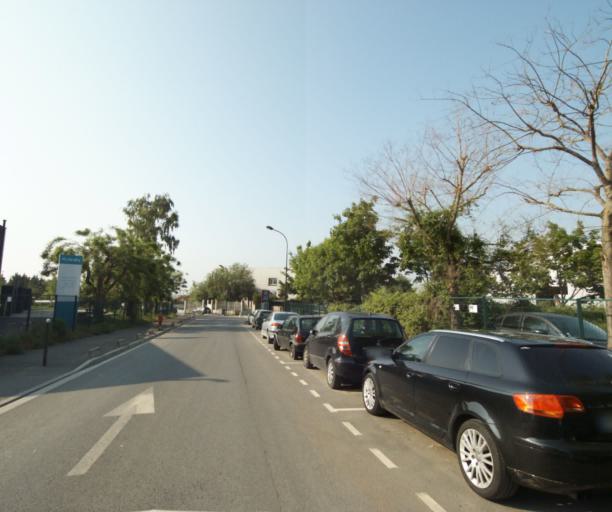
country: FR
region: Ile-de-France
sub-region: Departement des Yvelines
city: Sartrouville
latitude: 48.9547
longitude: 2.2067
